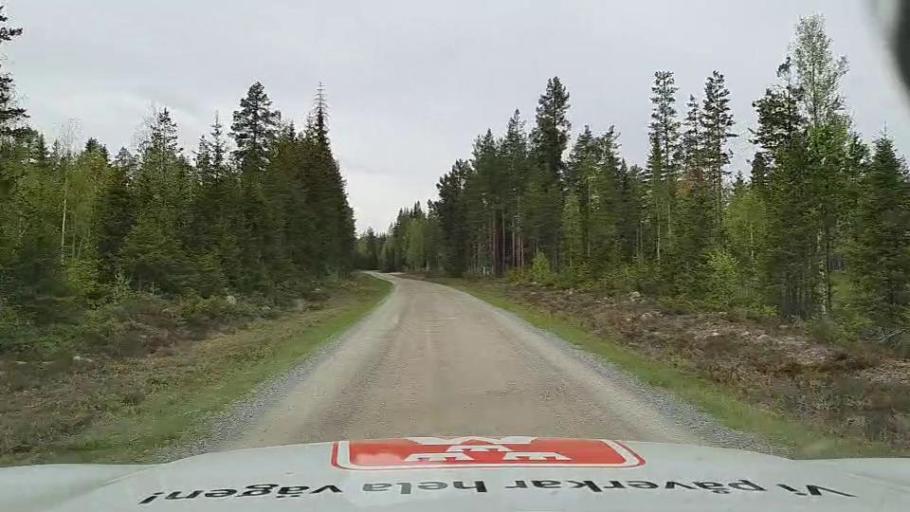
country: SE
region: Jaemtland
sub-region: Bergs Kommun
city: Hoverberg
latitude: 62.5041
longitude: 14.7025
